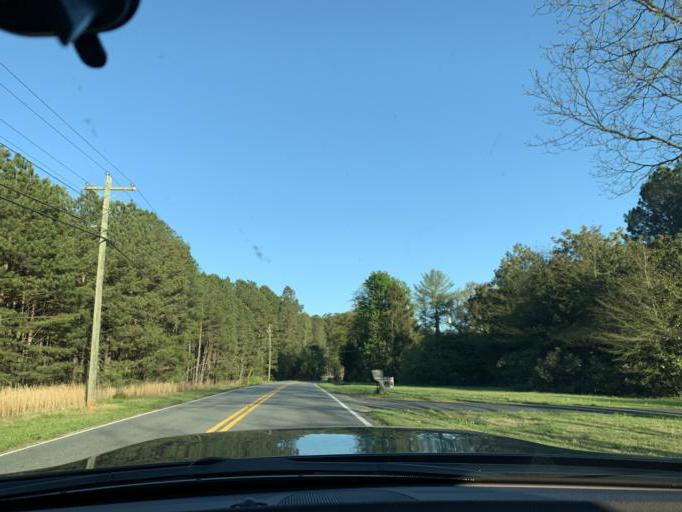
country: US
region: Georgia
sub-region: Forsyth County
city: Cumming
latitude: 34.2503
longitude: -84.1941
